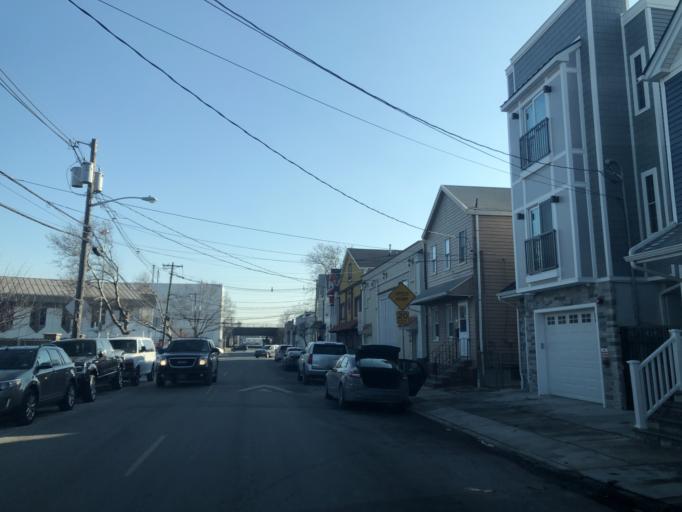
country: US
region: New Jersey
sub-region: Hudson County
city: Harrison
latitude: 40.7268
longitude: -74.1442
